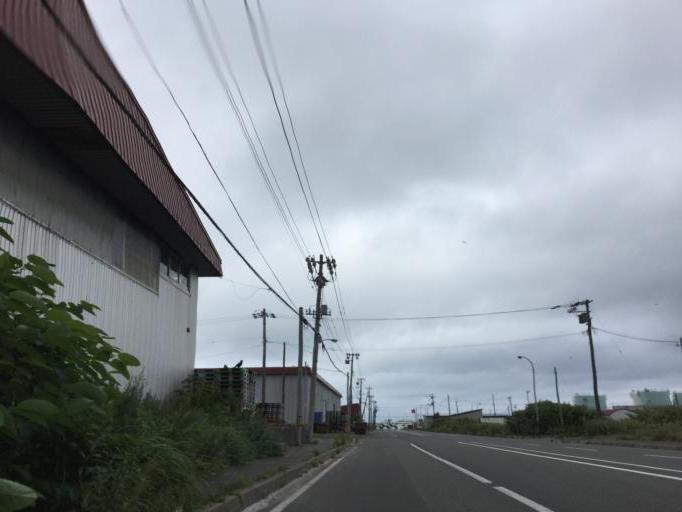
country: JP
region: Hokkaido
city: Wakkanai
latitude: 45.4059
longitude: 141.6822
